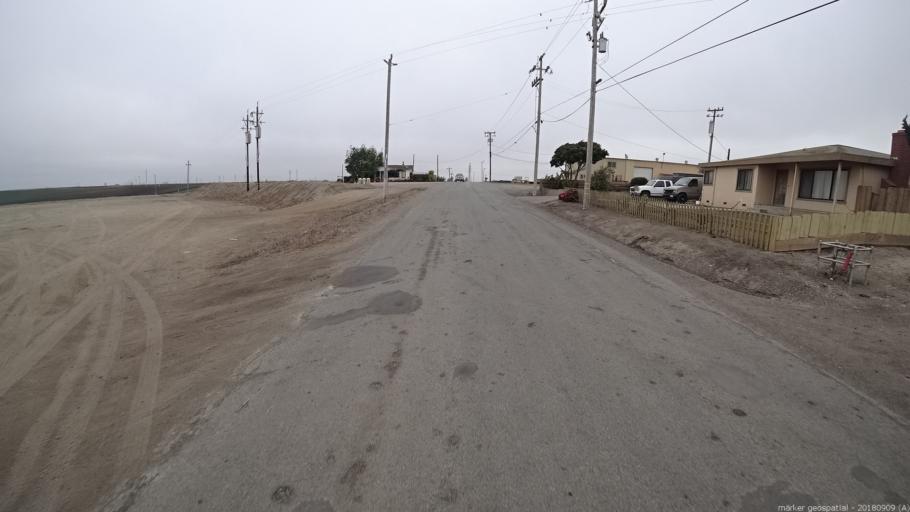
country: US
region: California
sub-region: Monterey County
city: Boronda
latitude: 36.7085
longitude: -121.7005
